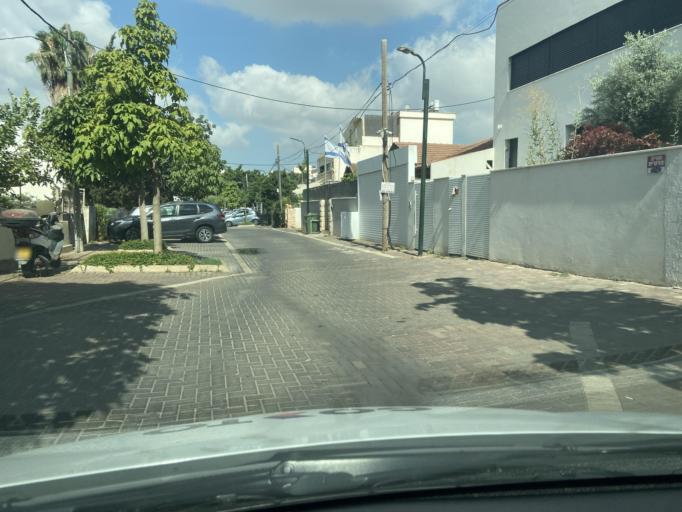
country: IL
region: Central District
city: Yehud
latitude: 32.0316
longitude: 34.8856
